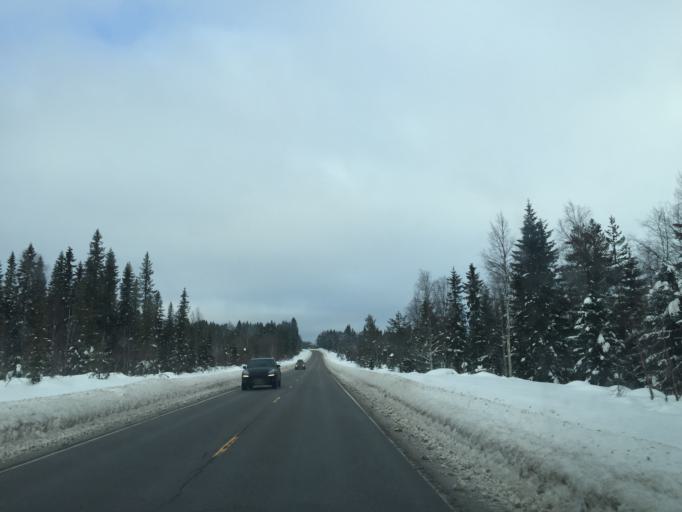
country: NO
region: Hedmark
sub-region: Trysil
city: Innbygda
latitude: 61.1280
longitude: 12.1028
